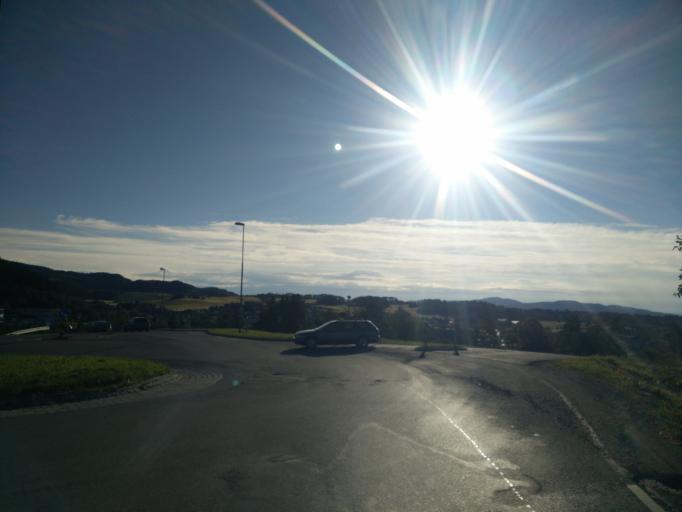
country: NO
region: Sor-Trondelag
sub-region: Klaebu
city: Klaebu
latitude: 63.4242
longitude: 10.5424
